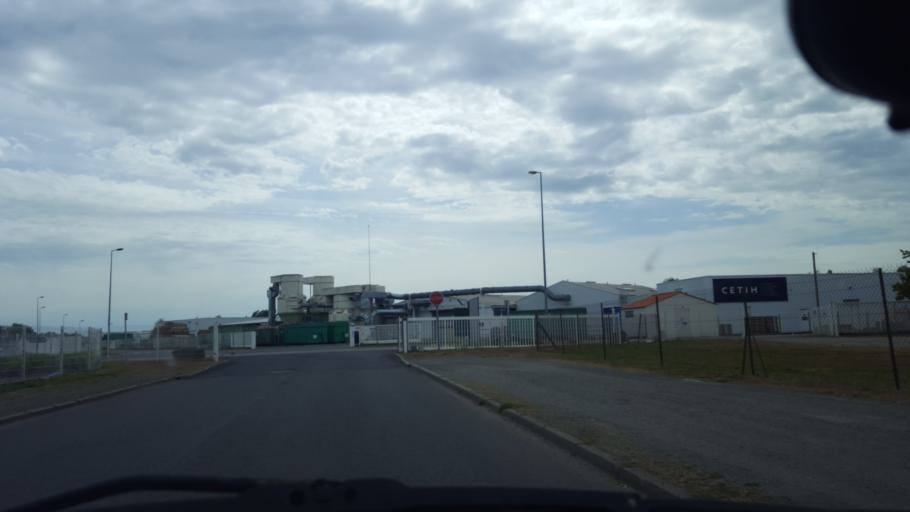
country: FR
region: Pays de la Loire
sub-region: Departement de la Loire-Atlantique
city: Machecoul
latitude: 46.9805
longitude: -1.8063
